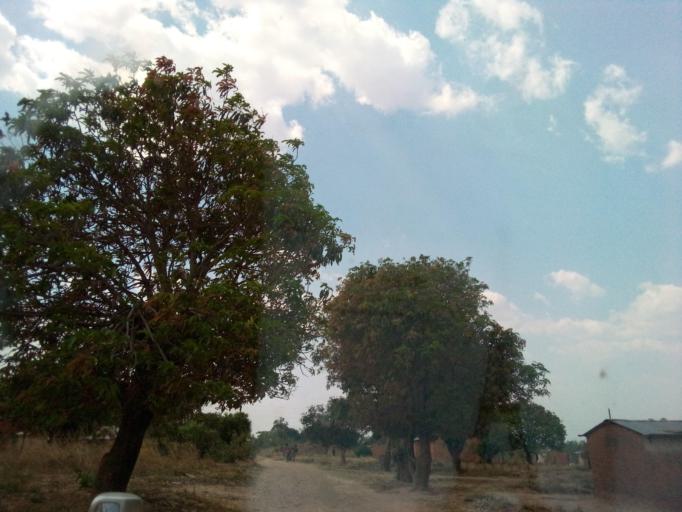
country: ZM
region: Northern
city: Mpika
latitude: -11.8342
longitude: 31.3879
